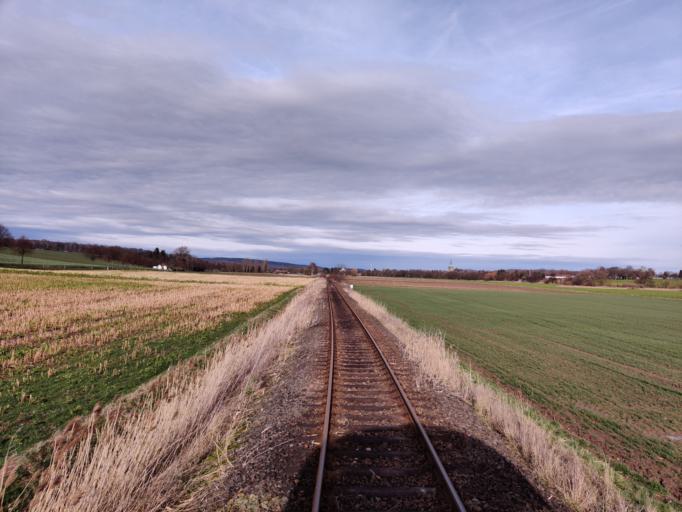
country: DE
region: Lower Saxony
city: Bockenem
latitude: 51.9947
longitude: 10.1226
